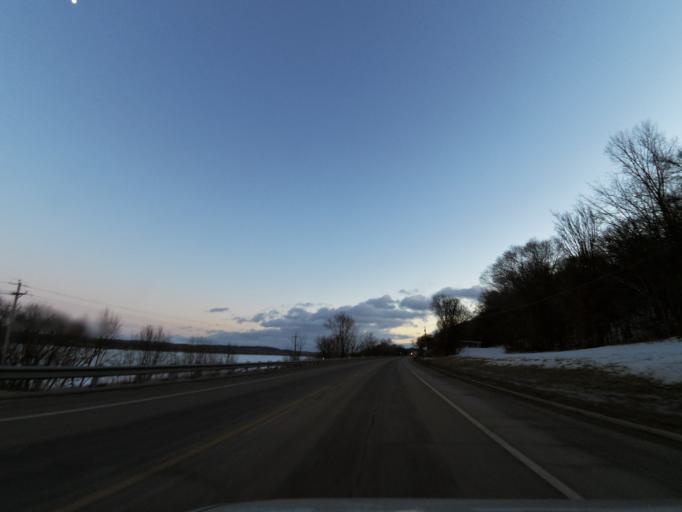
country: US
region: Minnesota
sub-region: Washington County
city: Bayport
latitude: 45.0034
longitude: -92.7792
